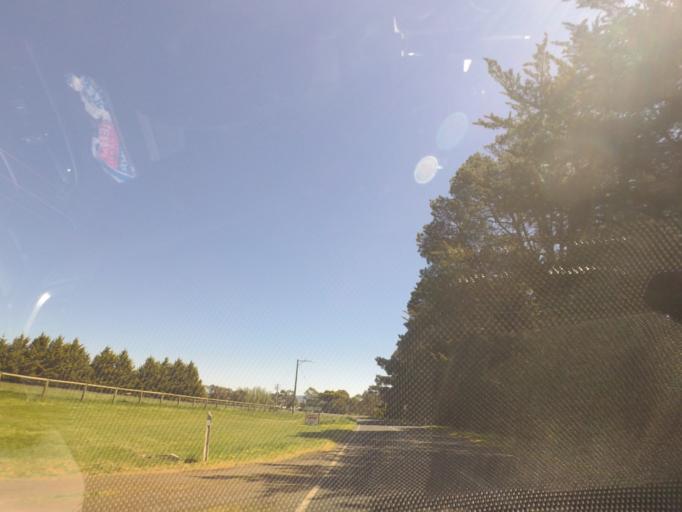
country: AU
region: Victoria
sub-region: Hume
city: Sunbury
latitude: -37.2784
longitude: 144.7464
